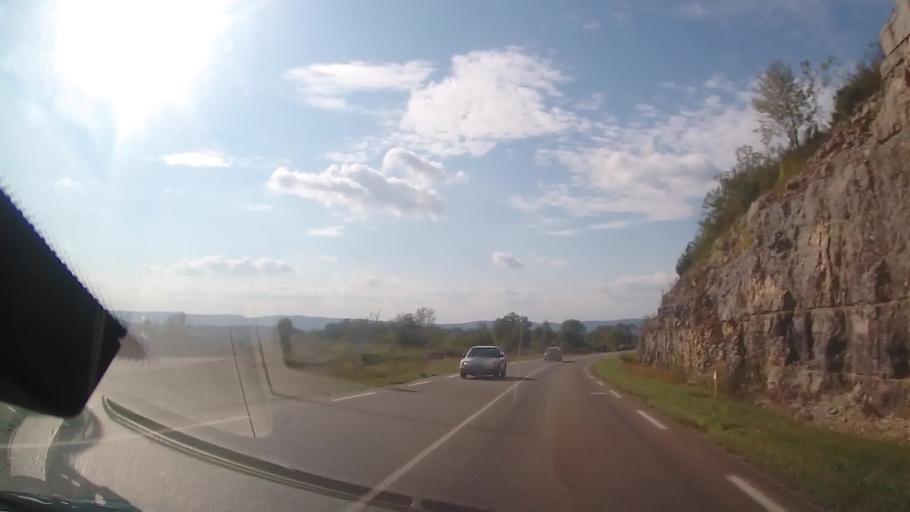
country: FR
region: Franche-Comte
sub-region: Departement du Jura
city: Clairvaux-les-Lacs
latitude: 46.5806
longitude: 5.7754
